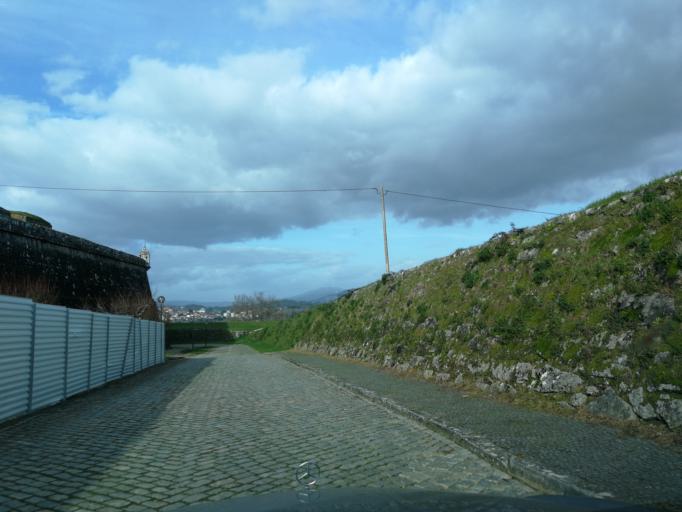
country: PT
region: Viana do Castelo
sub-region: Valenca
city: Valenca
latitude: 42.0316
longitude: -8.6435
